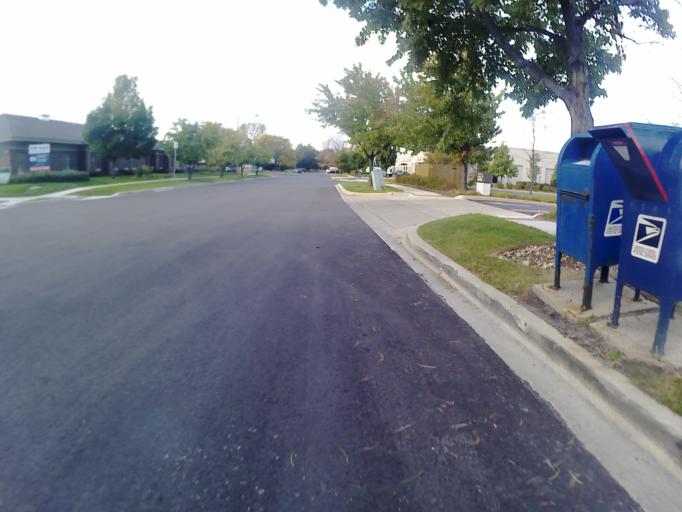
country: US
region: Illinois
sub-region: DuPage County
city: Lisle
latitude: 41.7863
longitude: -88.0812
